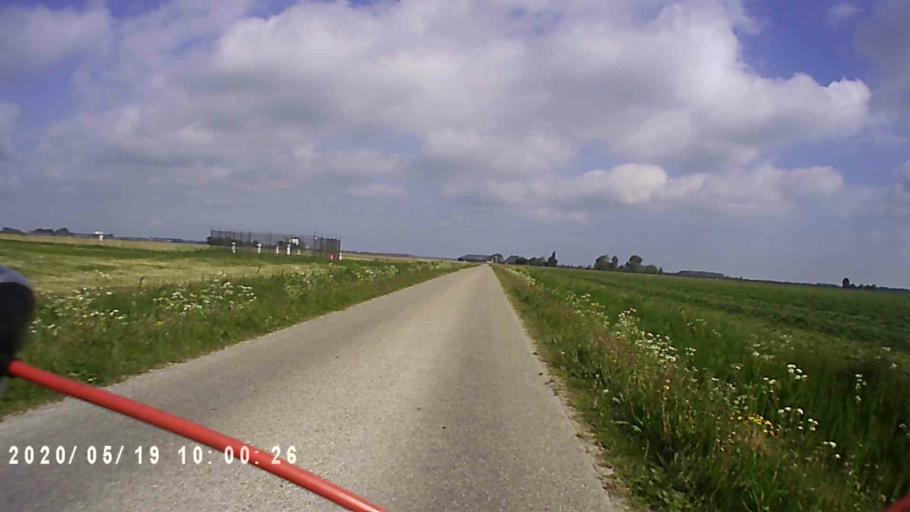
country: NL
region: Groningen
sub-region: Gemeente Zuidhorn
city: Grijpskerk
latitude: 53.2987
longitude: 6.2375
